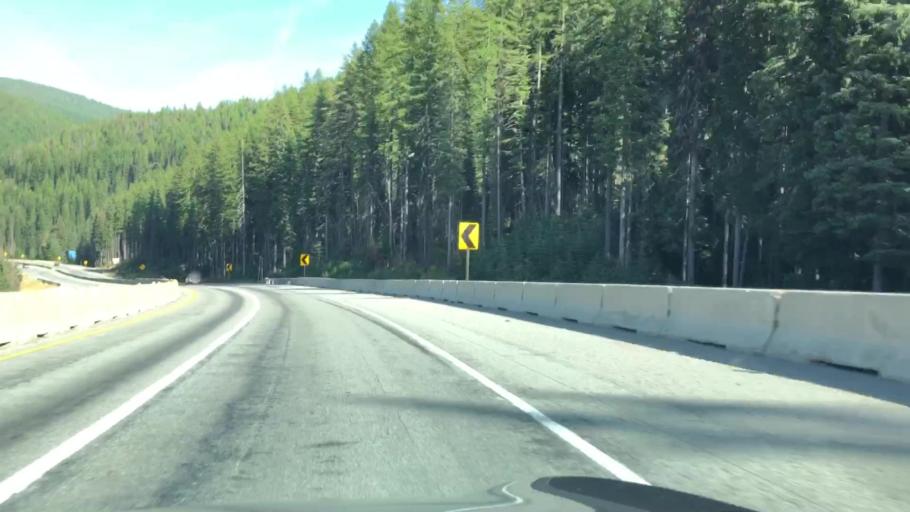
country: US
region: Idaho
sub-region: Shoshone County
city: Wallace
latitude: 47.4336
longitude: -115.6702
